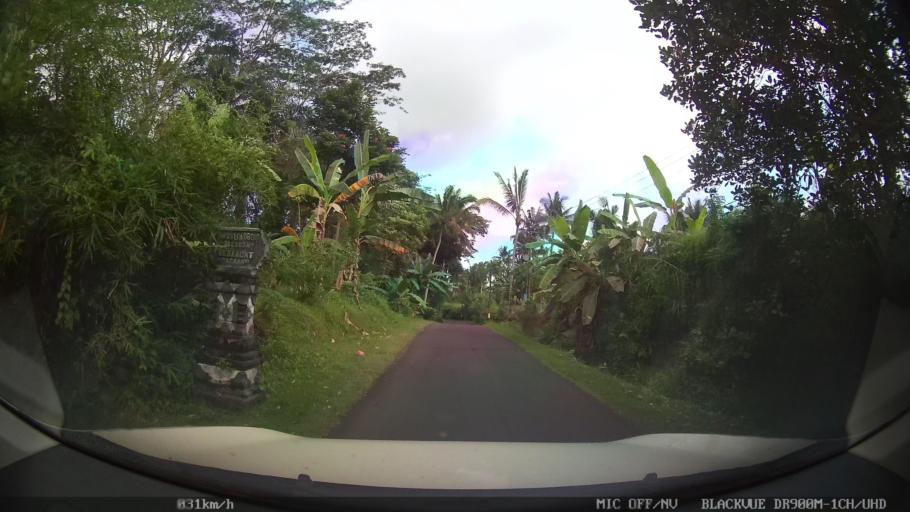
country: ID
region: Bali
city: Banjar Pesalakan
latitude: -8.4841
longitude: 115.2975
